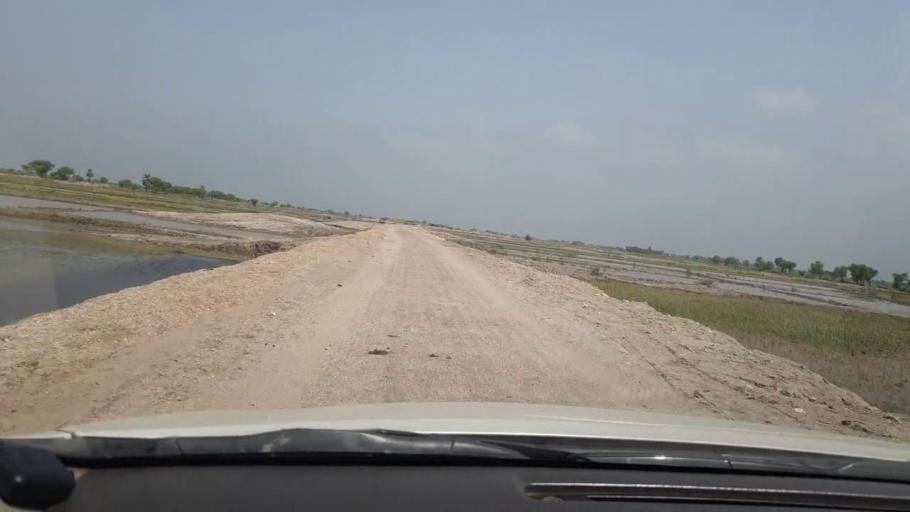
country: PK
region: Sindh
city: Shikarpur
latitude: 27.9966
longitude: 68.5615
